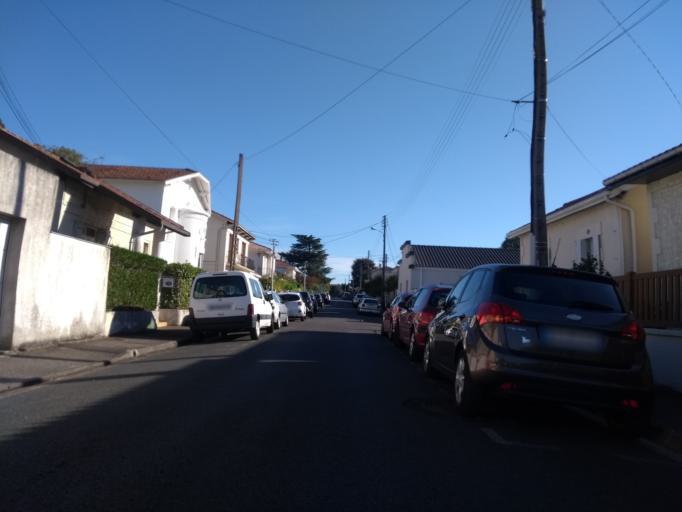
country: FR
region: Aquitaine
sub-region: Departement de la Gironde
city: Talence
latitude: 44.8141
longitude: -0.5981
